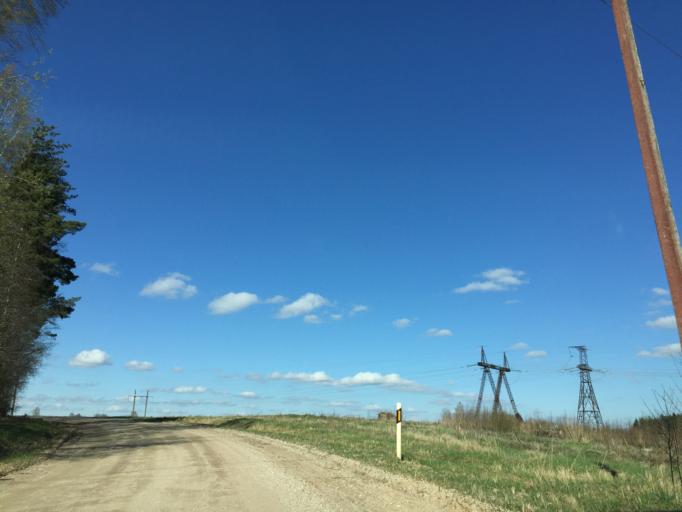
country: EE
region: Valgamaa
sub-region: Valga linn
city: Valga
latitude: 57.8514
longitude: 26.1702
